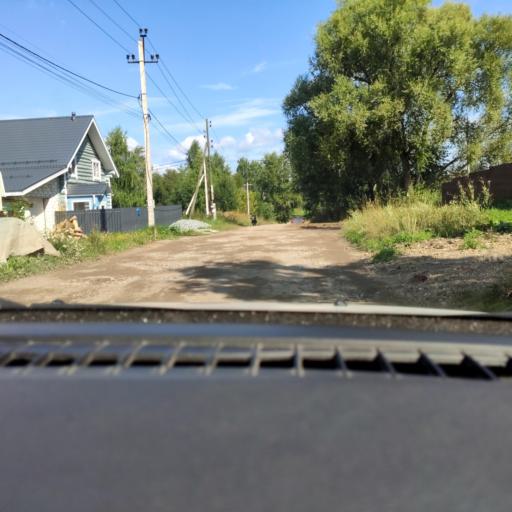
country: RU
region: Perm
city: Perm
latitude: 58.1140
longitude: 56.3906
